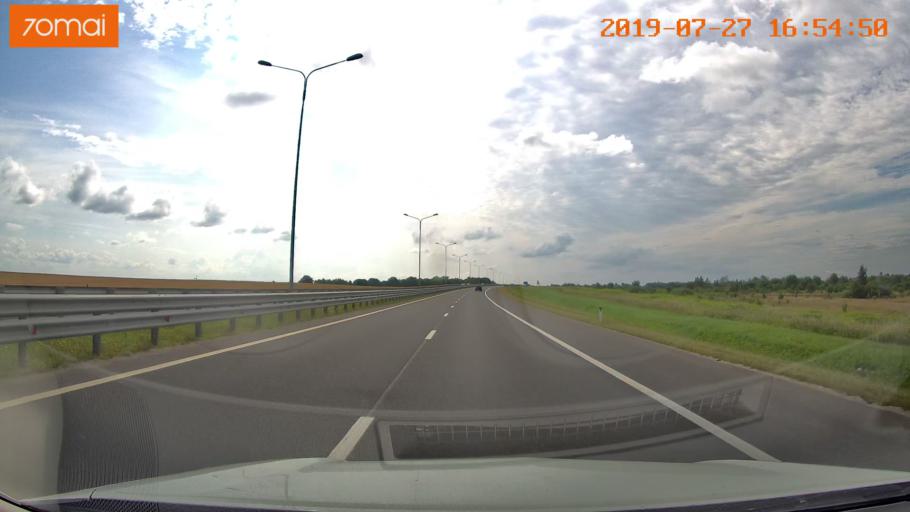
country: RU
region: Kaliningrad
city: Bol'shoe Isakovo
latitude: 54.6924
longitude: 20.7918
